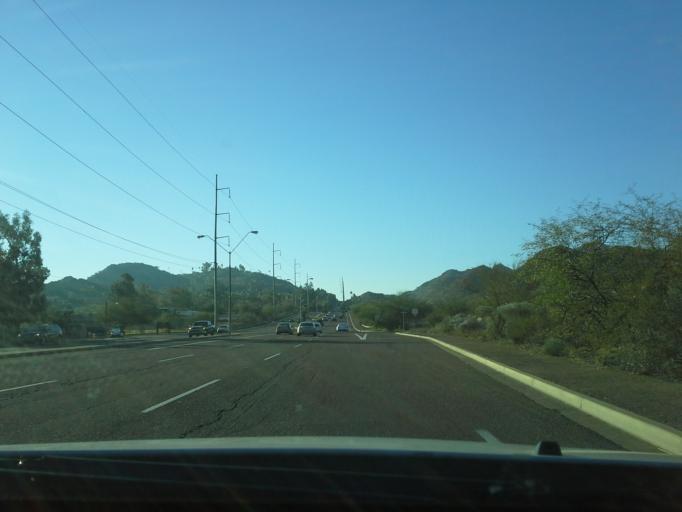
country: US
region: Arizona
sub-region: Maricopa County
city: Glendale
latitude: 33.6013
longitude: -112.0654
